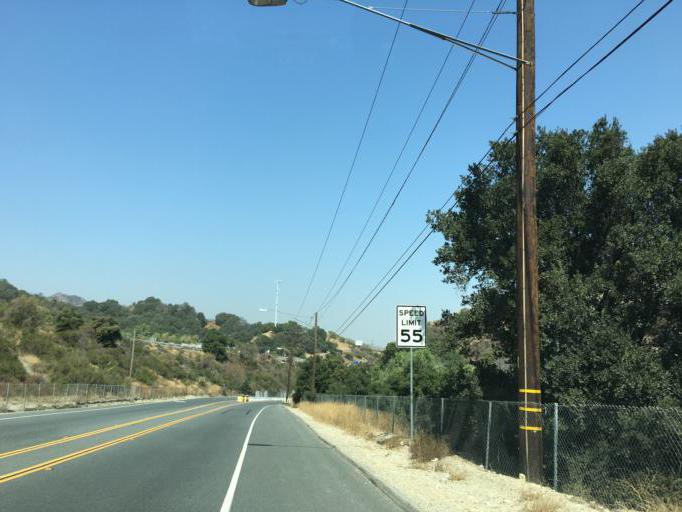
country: US
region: California
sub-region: Los Angeles County
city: Santa Clarita
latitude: 34.3422
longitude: -118.5257
